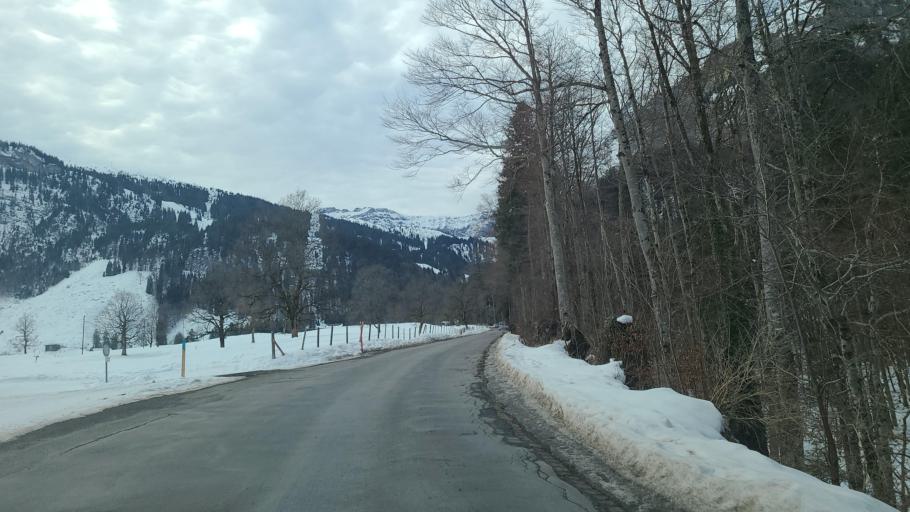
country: CH
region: Obwalden
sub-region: Obwalden
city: Sachseln
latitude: 46.8090
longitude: 8.2815
